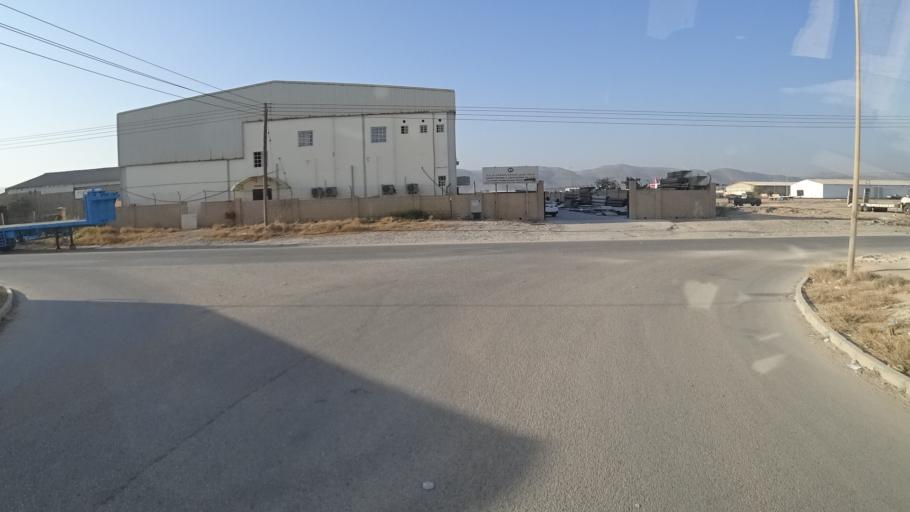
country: OM
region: Zufar
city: Salalah
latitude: 17.0243
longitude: 54.0447
